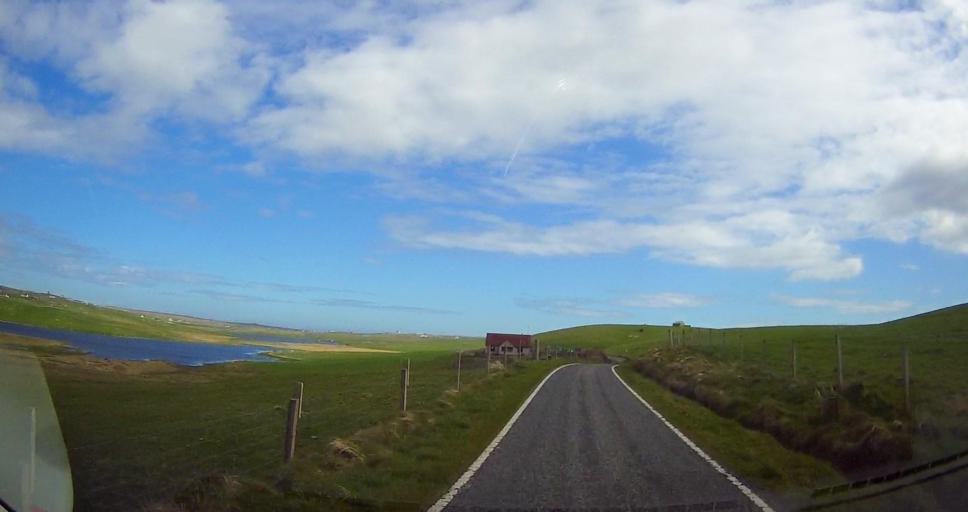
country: GB
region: Scotland
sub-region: Shetland Islands
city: Sandwick
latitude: 59.9265
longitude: -1.3444
